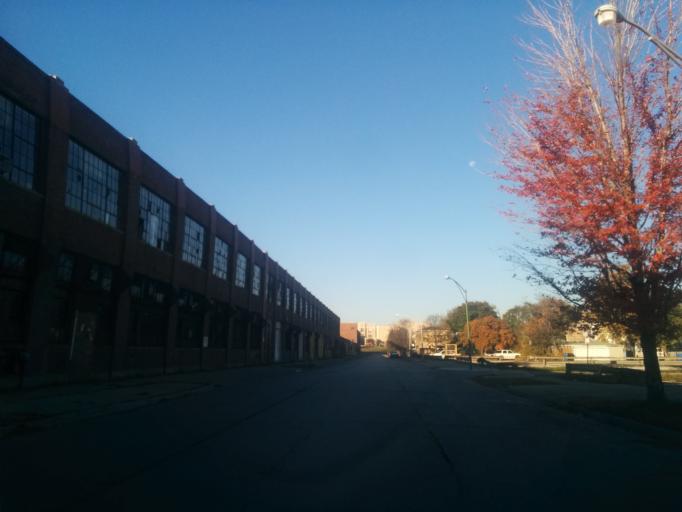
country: US
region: Illinois
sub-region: Cook County
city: Elmwood Park
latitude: 41.9180
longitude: -87.7763
